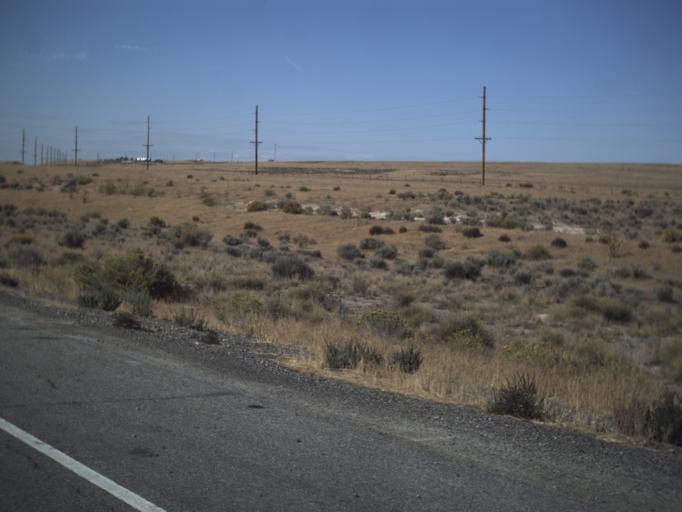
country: US
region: Utah
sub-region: Tooele County
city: Grantsville
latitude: 40.7687
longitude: -112.9860
